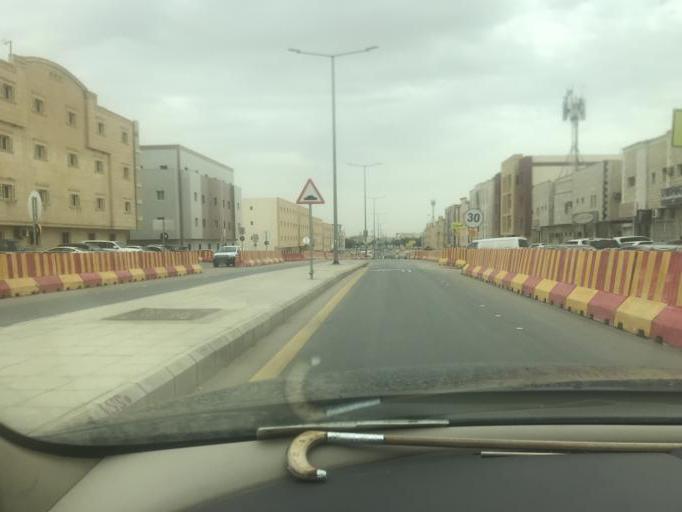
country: SA
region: Ar Riyad
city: Riyadh
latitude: 24.7926
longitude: 46.7102
